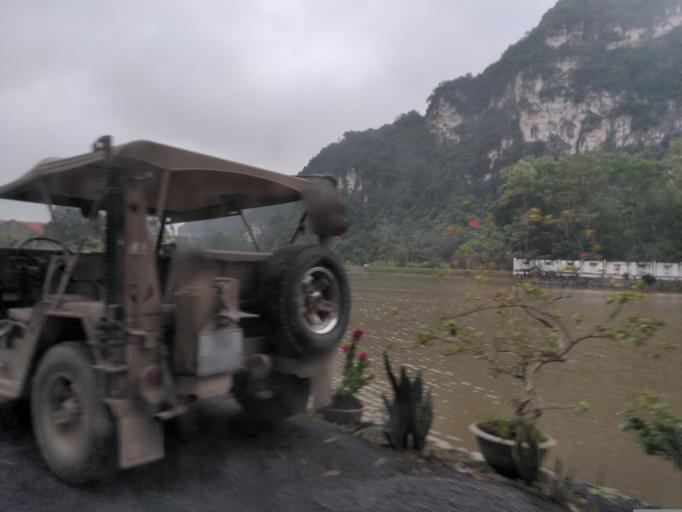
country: VN
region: Ninh Binh
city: Thi Tran Tam Diep
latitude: 20.2107
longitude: 105.9080
